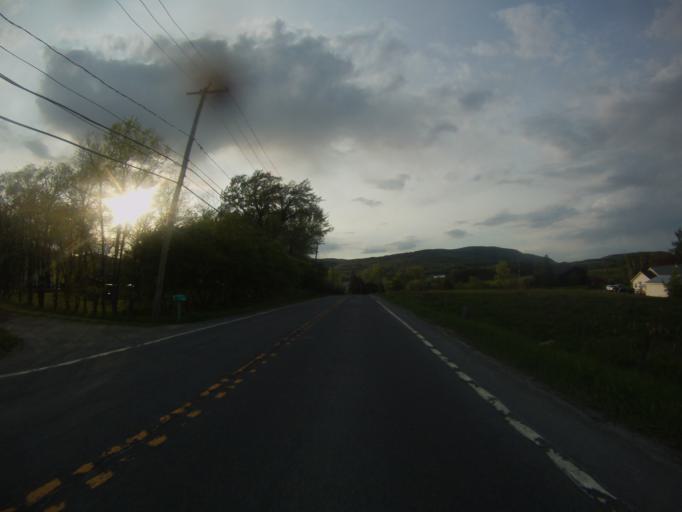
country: US
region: New York
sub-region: Essex County
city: Ticonderoga
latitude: 43.8706
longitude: -73.4422
